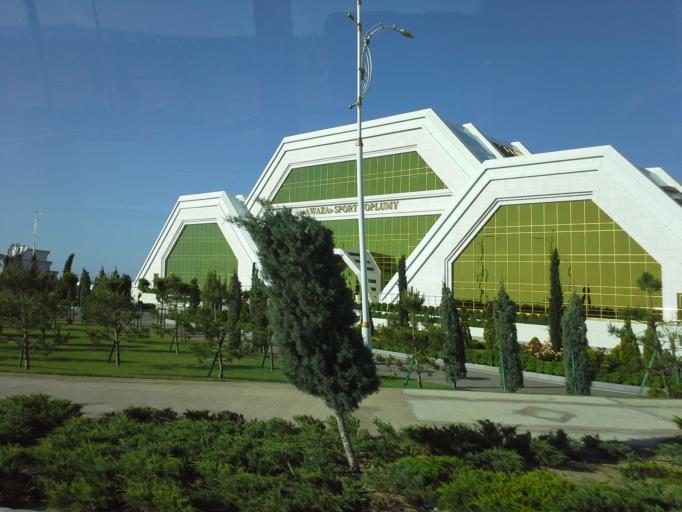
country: TM
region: Balkan
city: Turkmenbasy
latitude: 39.9469
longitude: 52.8837
